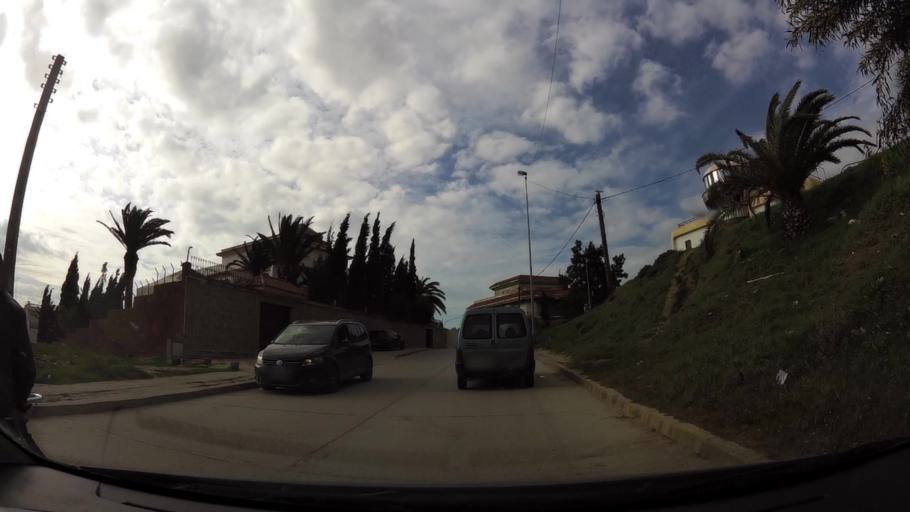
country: MA
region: Tanger-Tetouan
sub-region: Tanger-Assilah
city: Tangier
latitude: 35.7663
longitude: -5.7926
